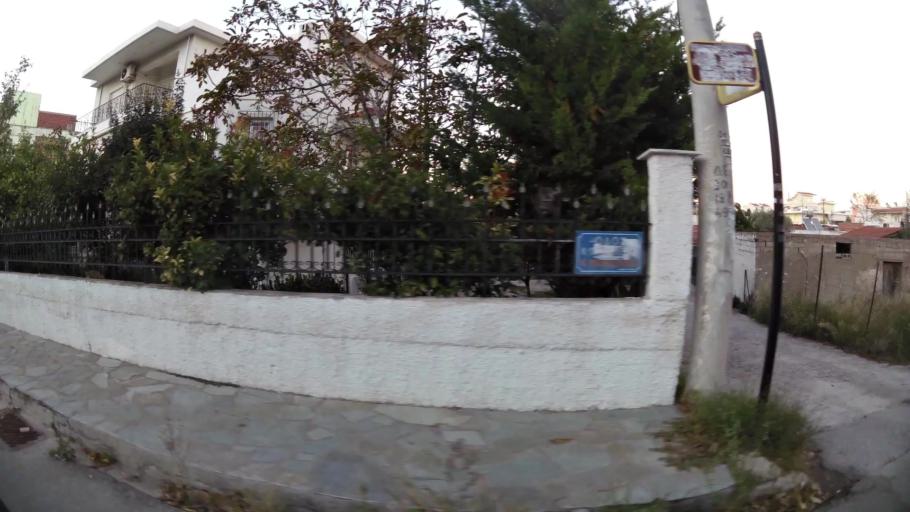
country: GR
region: Attica
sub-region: Nomarchia Anatolikis Attikis
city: Spata
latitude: 37.9662
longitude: 23.9145
